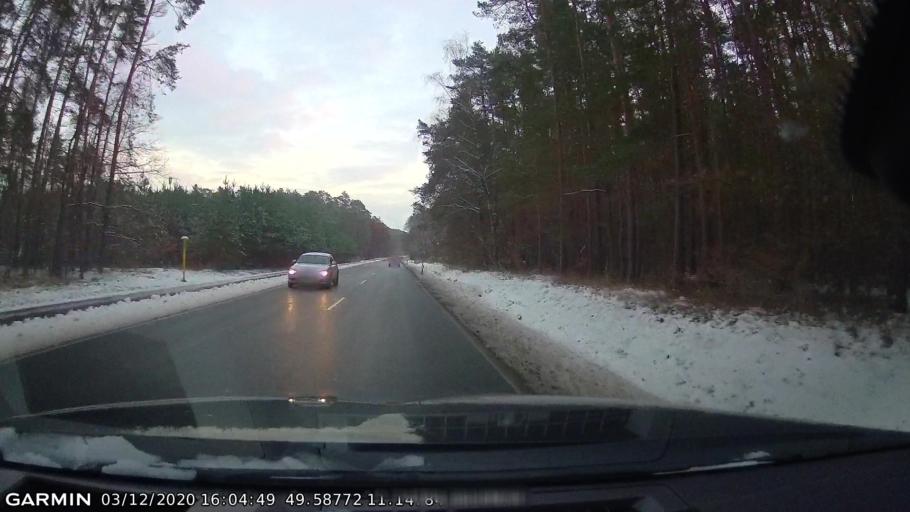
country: DE
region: Bavaria
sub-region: Upper Franconia
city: Kleinsendelbach
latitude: 49.5877
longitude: 11.1480
